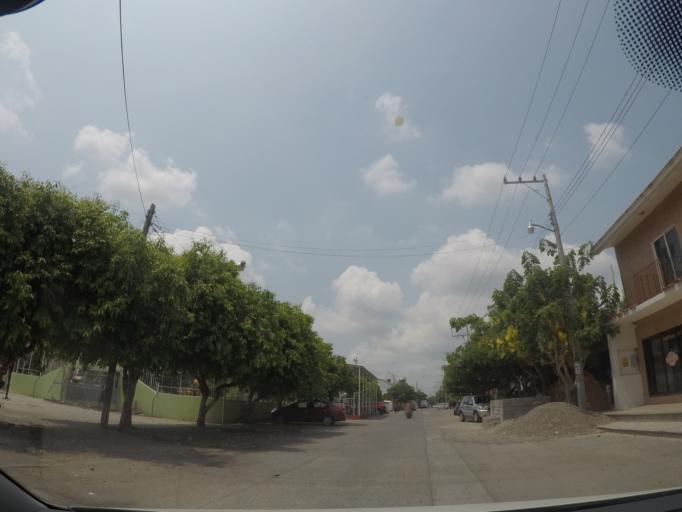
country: MX
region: Oaxaca
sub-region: El Espinal
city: El Espinal
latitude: 16.4858
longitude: -95.0440
